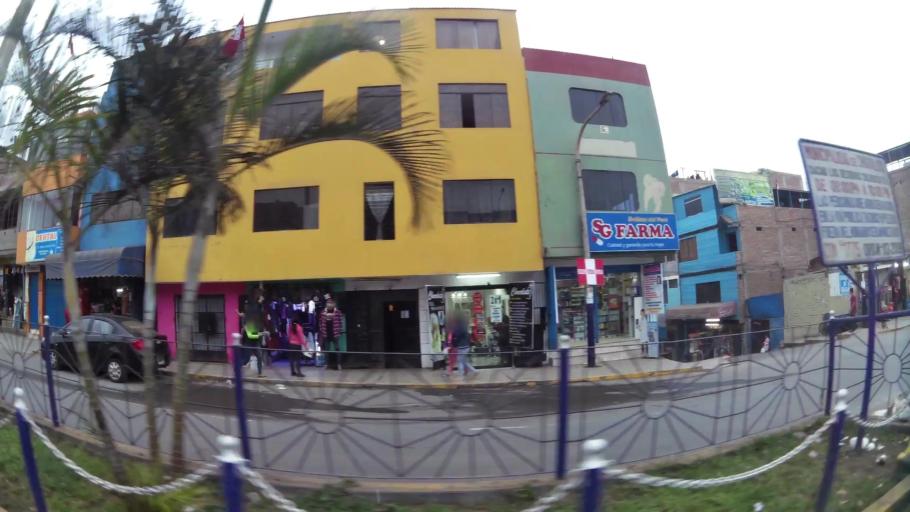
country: PE
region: Lima
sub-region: Lima
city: Surco
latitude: -12.1939
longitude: -77.0203
